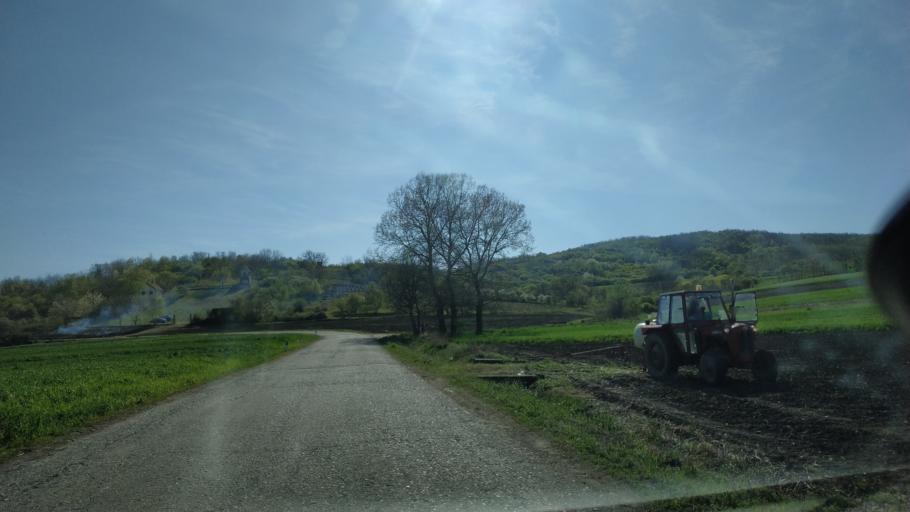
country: RS
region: Central Serbia
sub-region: Nisavski Okrug
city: Aleksinac
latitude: 43.4997
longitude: 21.6759
